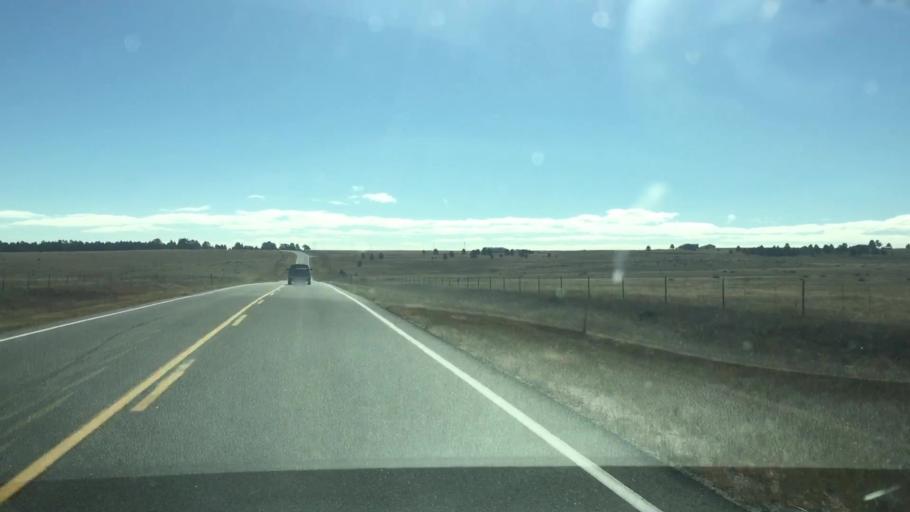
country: US
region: Colorado
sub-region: Elbert County
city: Kiowa
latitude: 39.3364
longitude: -104.4269
